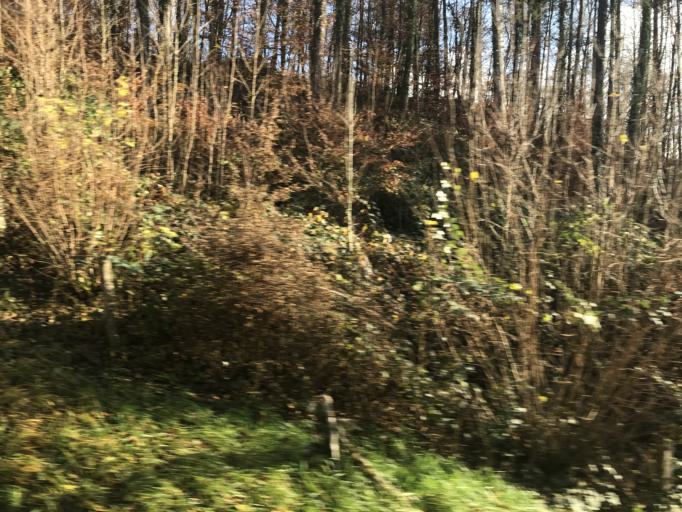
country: CH
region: Schaffhausen
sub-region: Bezirk Schaffhausen
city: Neuhausen
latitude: 47.6766
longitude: 8.6071
